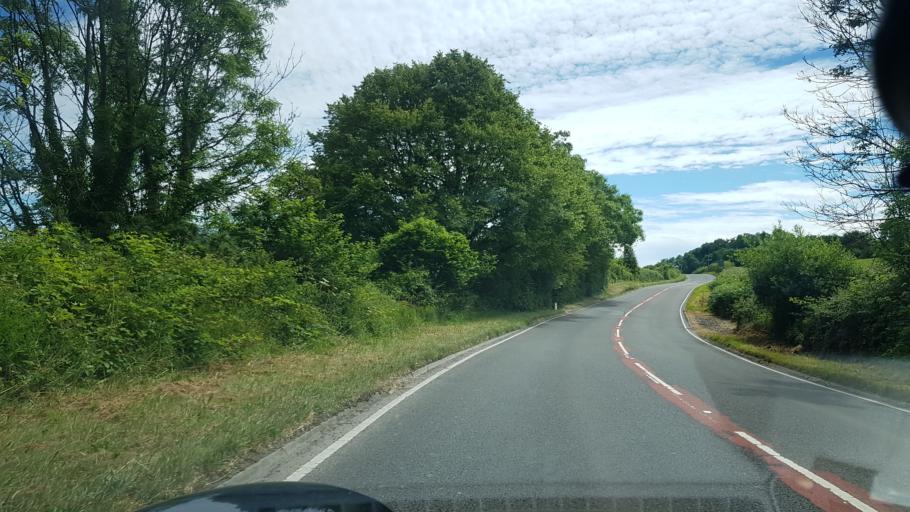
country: GB
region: Wales
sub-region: Carmarthenshire
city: Saint Clears
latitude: 51.8034
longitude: -4.4952
